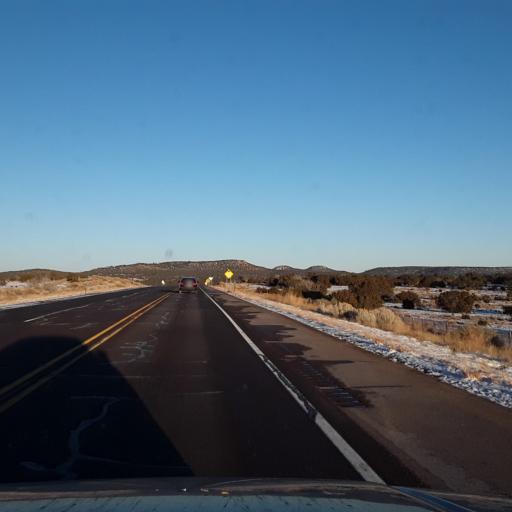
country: US
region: New Mexico
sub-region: Lincoln County
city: Carrizozo
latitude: 34.2364
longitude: -105.6122
